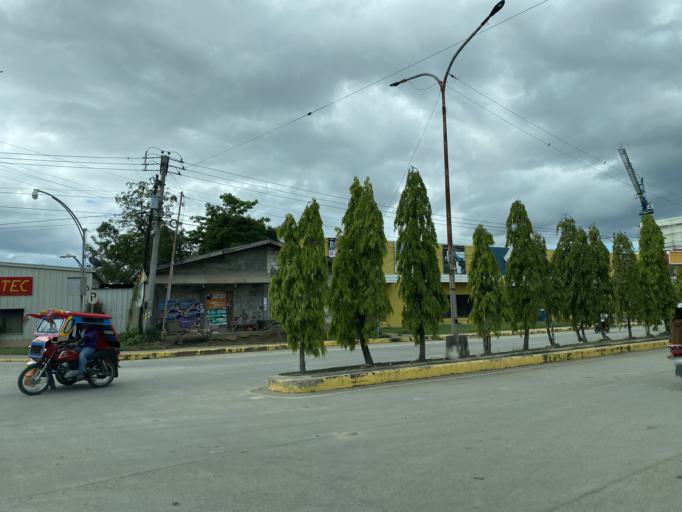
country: PH
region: Central Visayas
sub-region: Province of Bohol
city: Tagbilaran City
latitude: 9.6548
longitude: 123.8726
